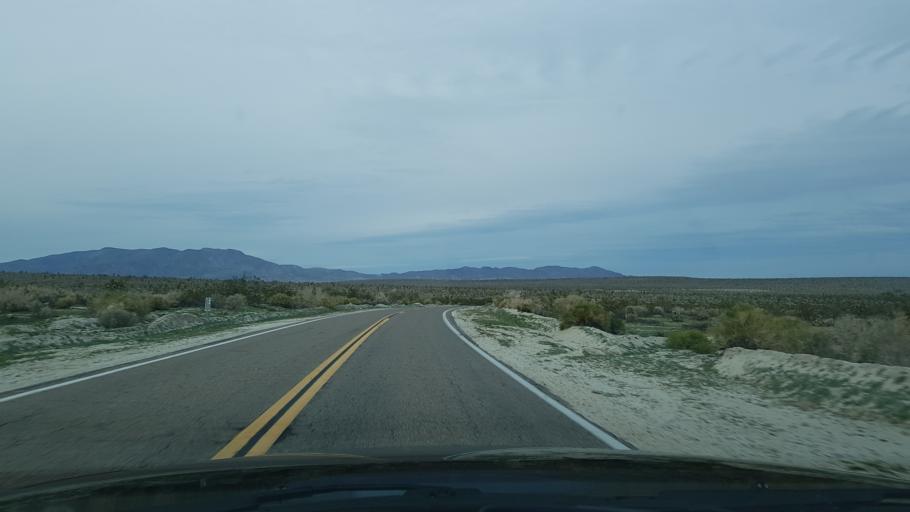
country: US
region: California
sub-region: San Diego County
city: Pine Valley
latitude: 32.8622
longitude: -116.2099
